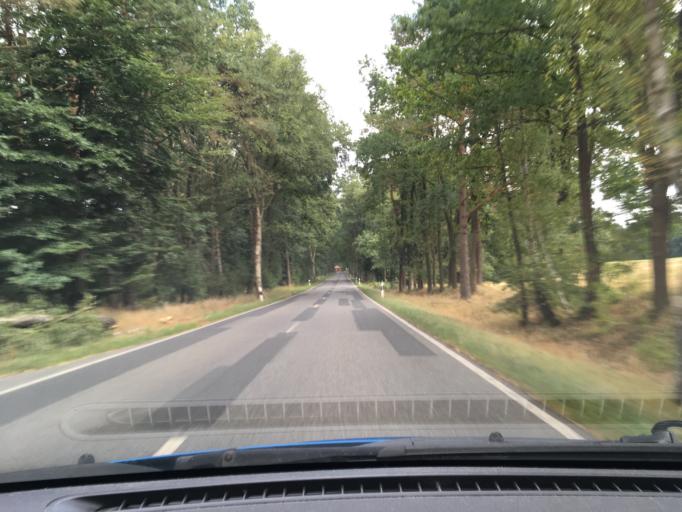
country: DE
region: Lower Saxony
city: Undeloh
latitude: 53.2005
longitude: 9.9665
